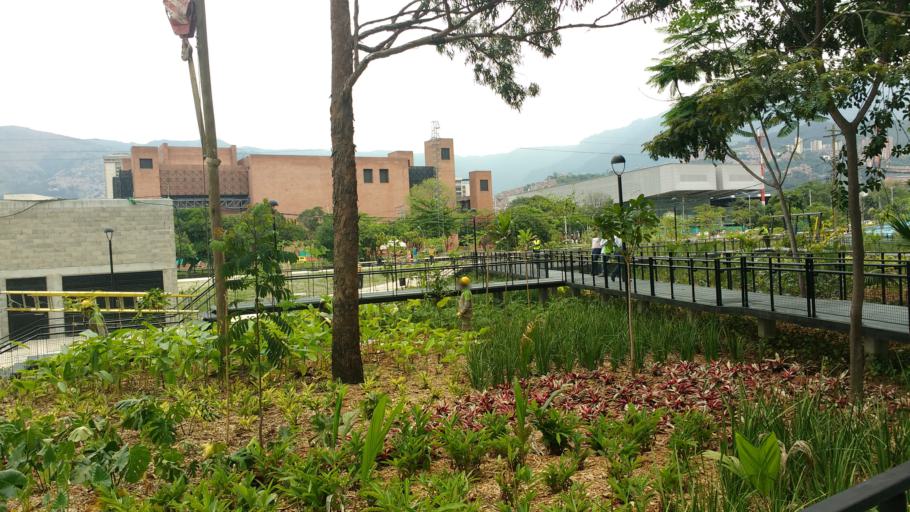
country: CO
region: Antioquia
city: Medellin
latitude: 6.2429
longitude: -75.5795
